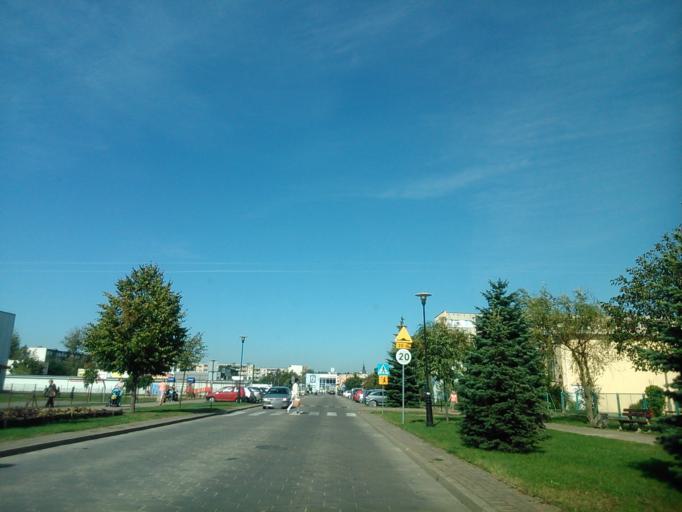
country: PL
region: Kujawsko-Pomorskie
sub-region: Powiat golubsko-dobrzynski
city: Golub-Dobrzyn
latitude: 53.1027
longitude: 19.0565
